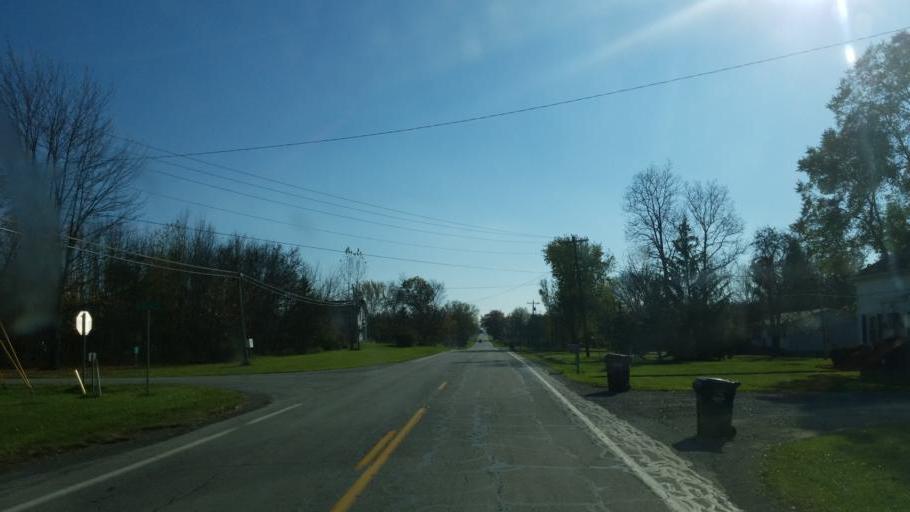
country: US
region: Ohio
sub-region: Lorain County
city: Wellington
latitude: 41.1167
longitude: -82.2197
